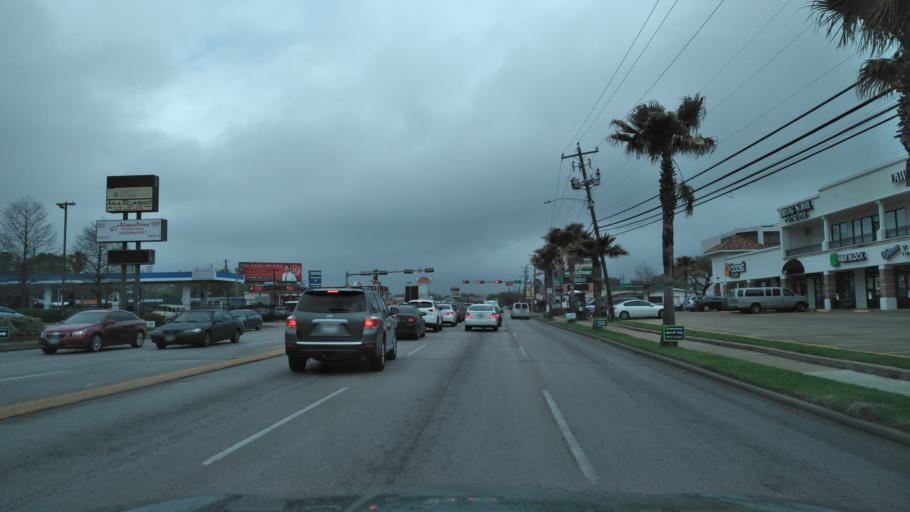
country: US
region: Texas
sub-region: Harris County
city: Piney Point Village
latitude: 29.7305
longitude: -95.5011
